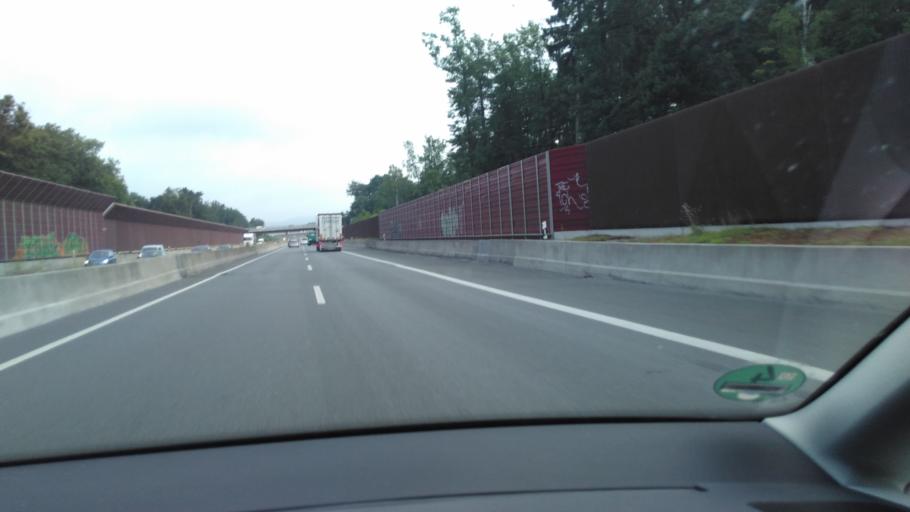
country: DE
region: North Rhine-Westphalia
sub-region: Regierungsbezirk Detmold
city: Verl
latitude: 51.9526
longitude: 8.5058
